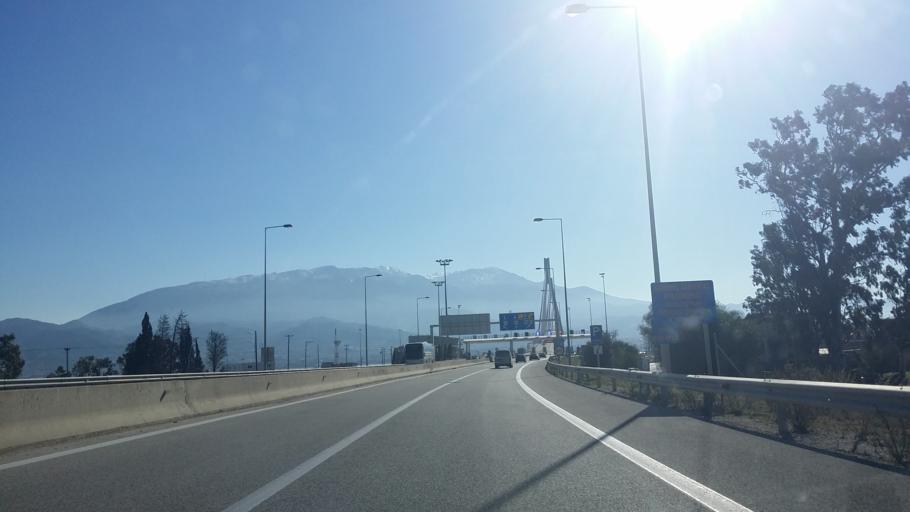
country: GR
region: West Greece
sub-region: Nomos Aitolias kai Akarnanias
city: Antirrio
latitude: 38.3371
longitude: 21.7640
